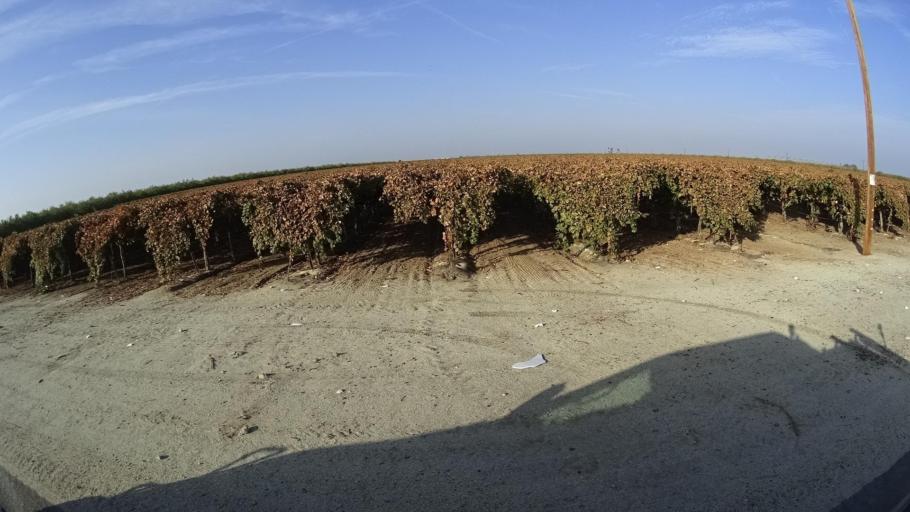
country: US
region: California
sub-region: Kern County
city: McFarland
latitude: 35.7152
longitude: -119.1872
